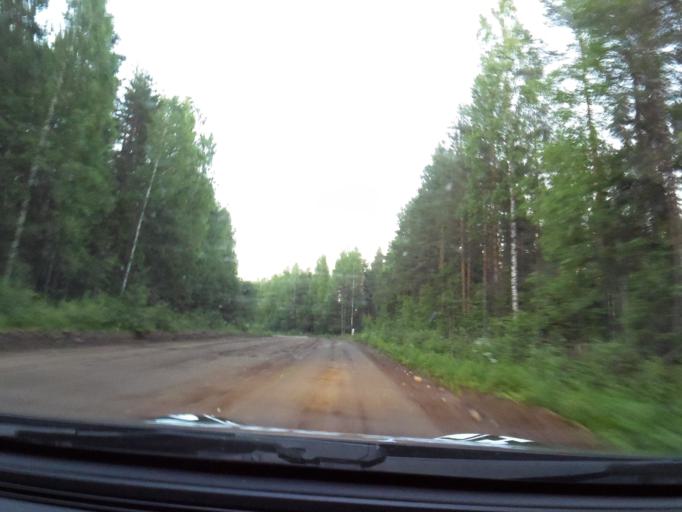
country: RU
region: Leningrad
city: Voznesen'ye
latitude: 60.8547
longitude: 35.9098
